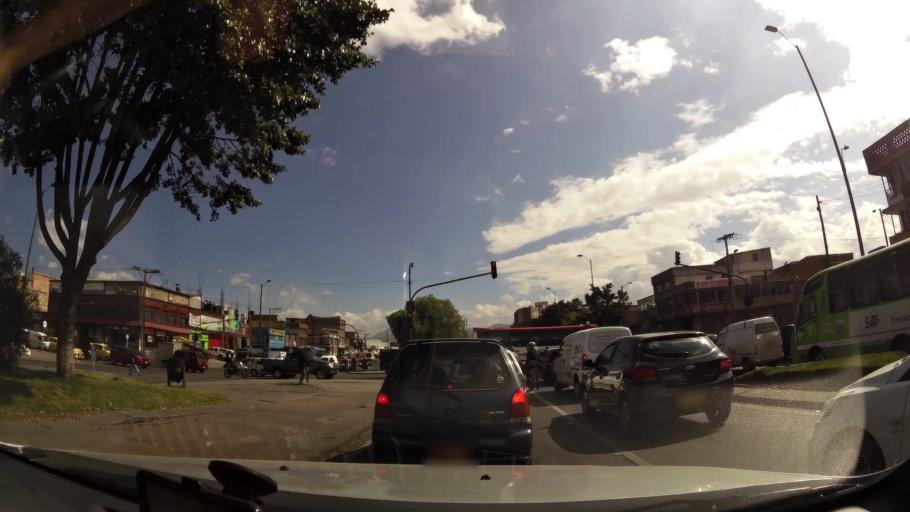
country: CO
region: Bogota D.C.
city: Bogota
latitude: 4.6067
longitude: -74.1420
